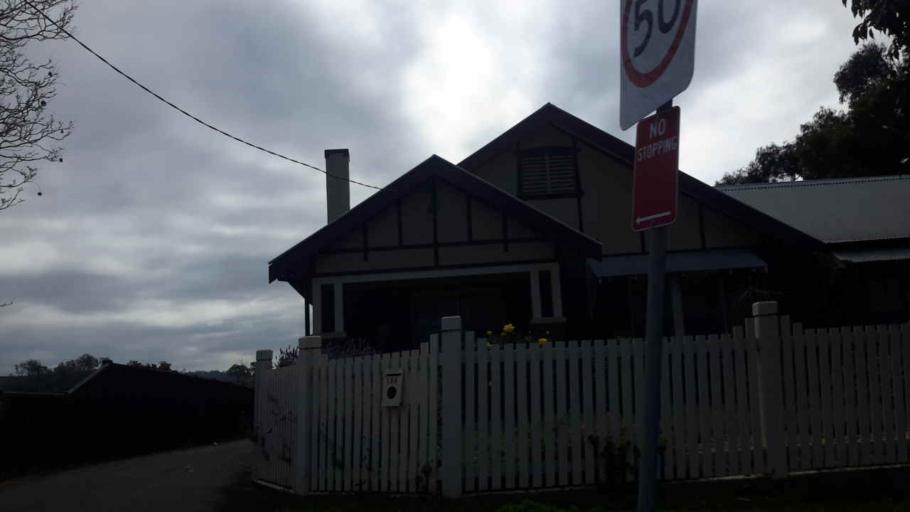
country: AU
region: New South Wales
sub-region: Camden
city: Camden South
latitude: -34.1265
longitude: 150.7386
